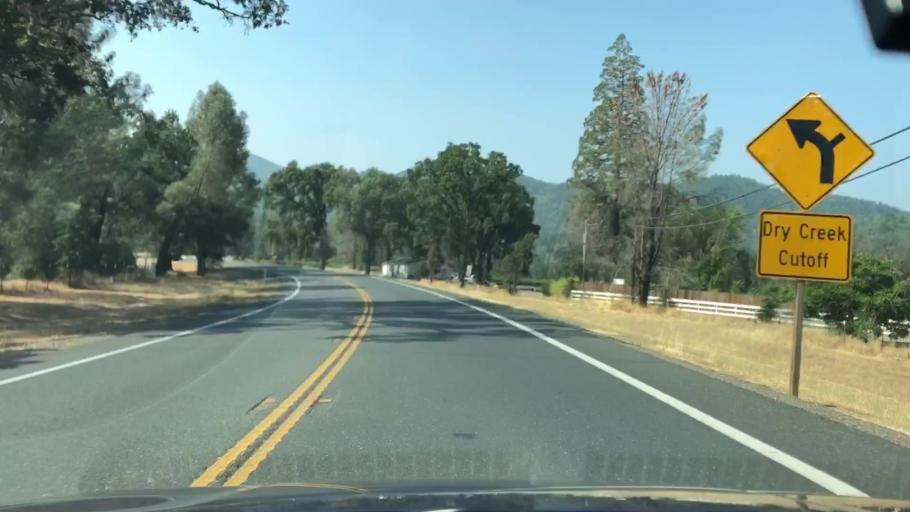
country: US
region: California
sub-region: Lake County
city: Middletown
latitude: 38.7394
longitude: -122.6259
